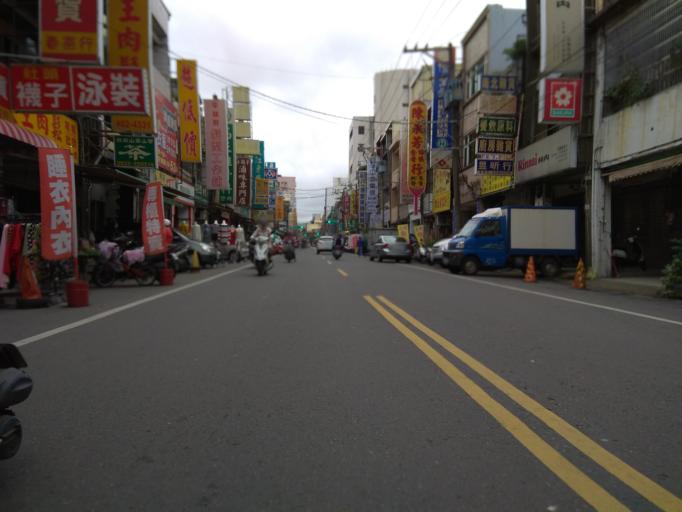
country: TW
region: Taiwan
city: Taoyuan City
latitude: 24.9571
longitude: 121.2148
